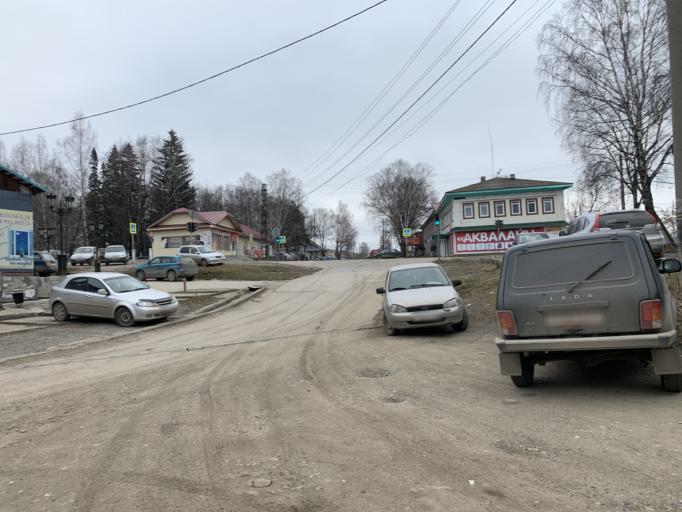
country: RU
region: Chelyabinsk
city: Nyazepetrovsk
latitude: 56.0528
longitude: 59.5914
